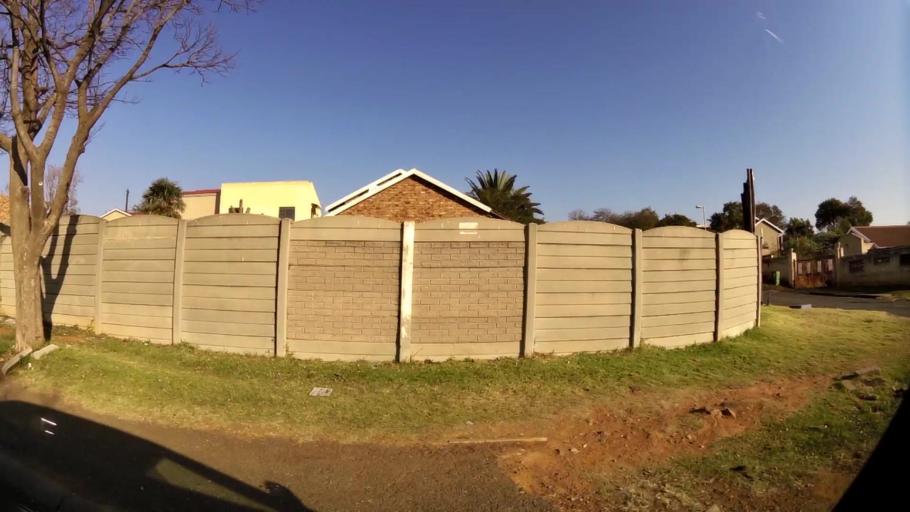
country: ZA
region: Gauteng
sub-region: City of Johannesburg Metropolitan Municipality
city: Soweto
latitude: -26.2800
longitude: 27.9615
